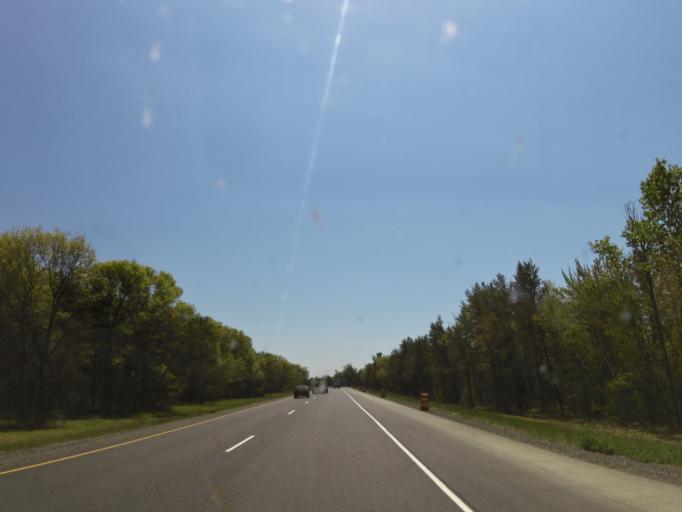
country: US
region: Wisconsin
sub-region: Jackson County
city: Black River Falls
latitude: 44.2511
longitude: -90.7536
